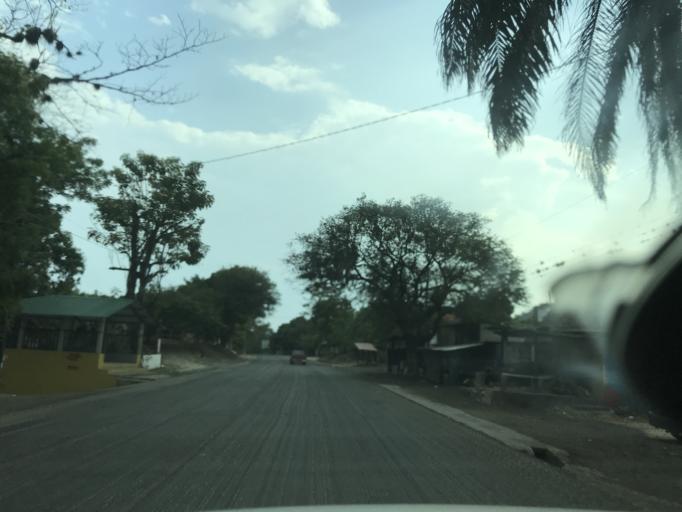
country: GT
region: Zacapa
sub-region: Municipio de Zacapa
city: Gualan
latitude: 15.1743
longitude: -89.3050
